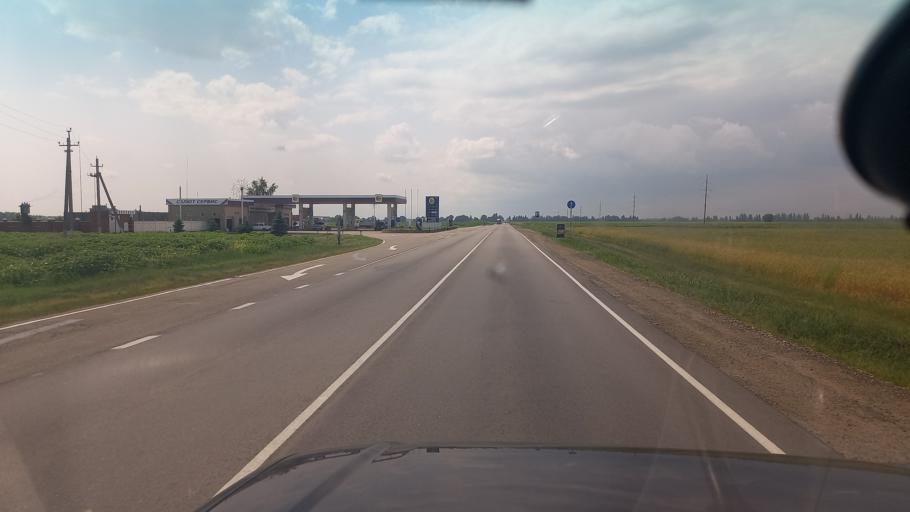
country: RU
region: Adygeya
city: Koshekhabl'
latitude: 44.9034
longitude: 40.4714
